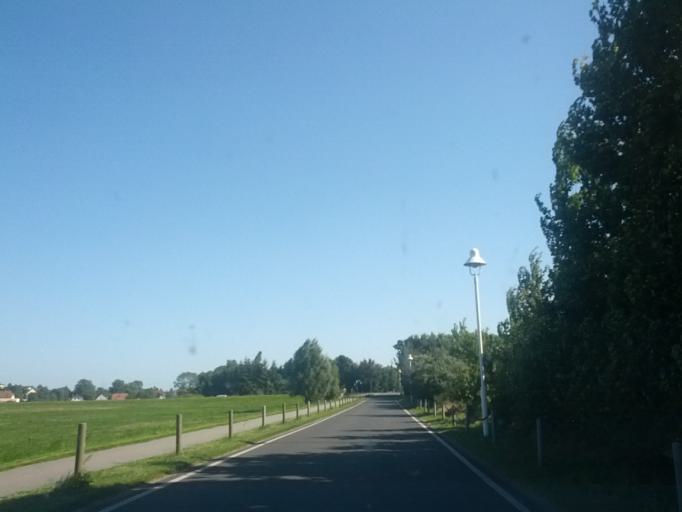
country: DE
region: Mecklenburg-Vorpommern
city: Ostseebad Gohren
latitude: 54.2763
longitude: 13.7042
